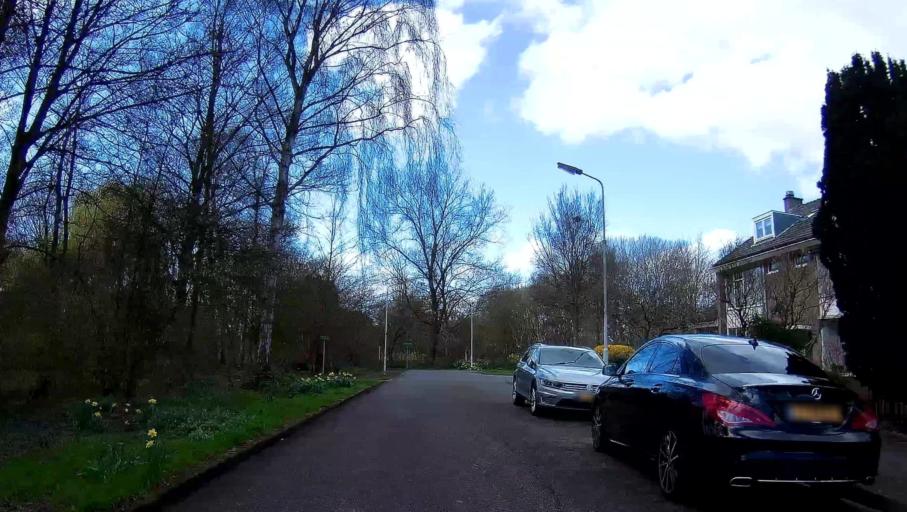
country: NL
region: South Holland
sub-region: Gemeente Zoetermeer
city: Zoetermeer
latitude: 52.0492
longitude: 4.4831
